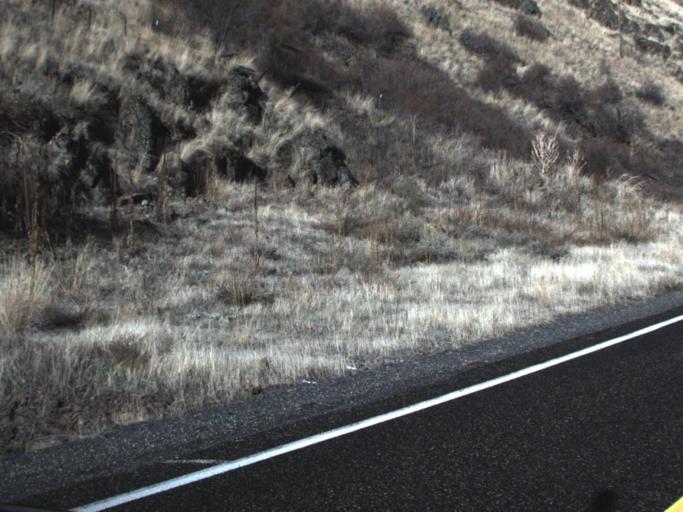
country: US
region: Washington
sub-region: Asotin County
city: Asotin
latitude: 46.0278
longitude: -117.2573
